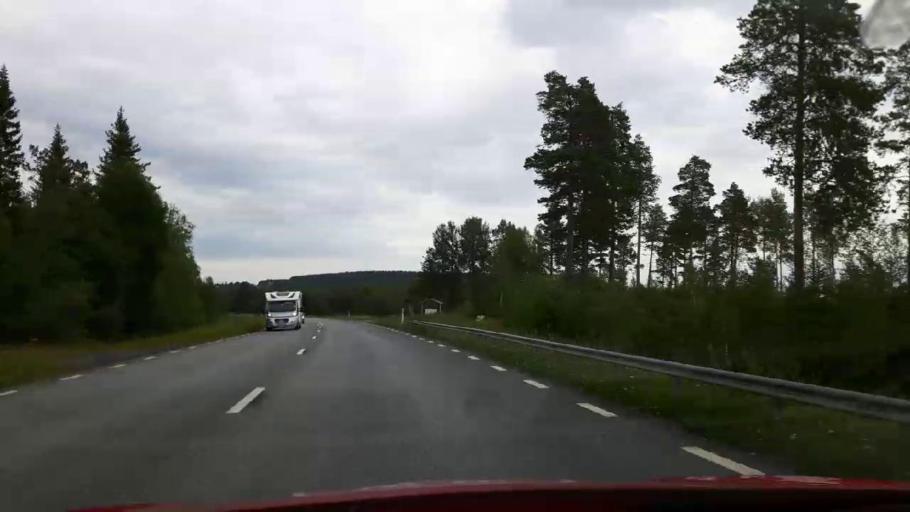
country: SE
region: Jaemtland
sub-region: Stroemsunds Kommun
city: Stroemsund
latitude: 63.5428
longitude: 15.3689
